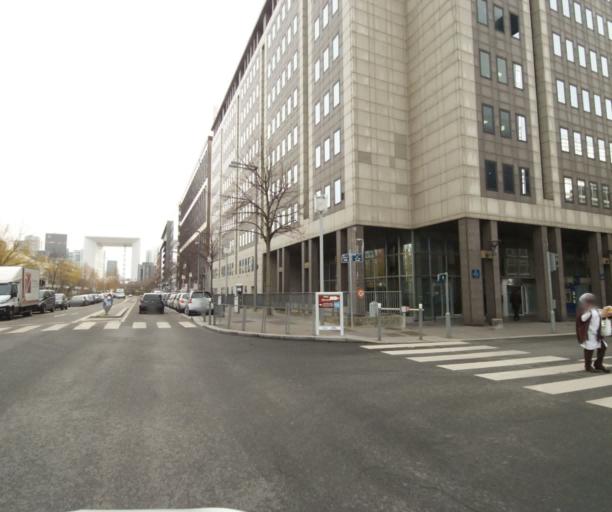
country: FR
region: Ile-de-France
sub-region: Departement des Hauts-de-Seine
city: La Defense
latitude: 48.8958
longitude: 2.2242
